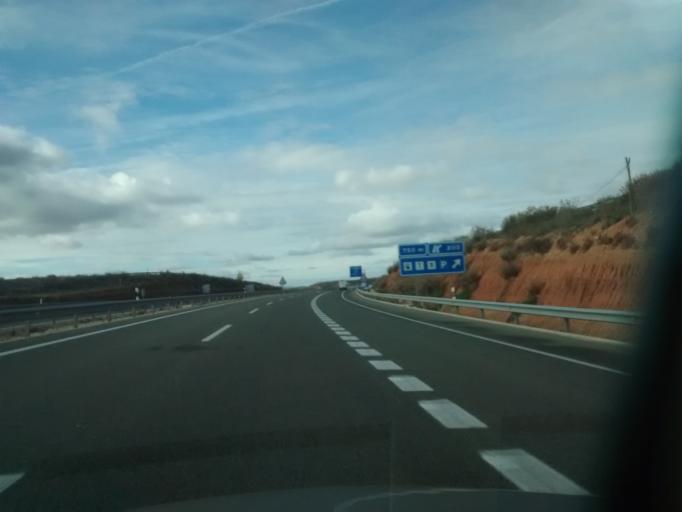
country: ES
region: Aragon
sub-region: Provincia de Zaragoza
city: Cetina
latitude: 41.3028
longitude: -1.9538
